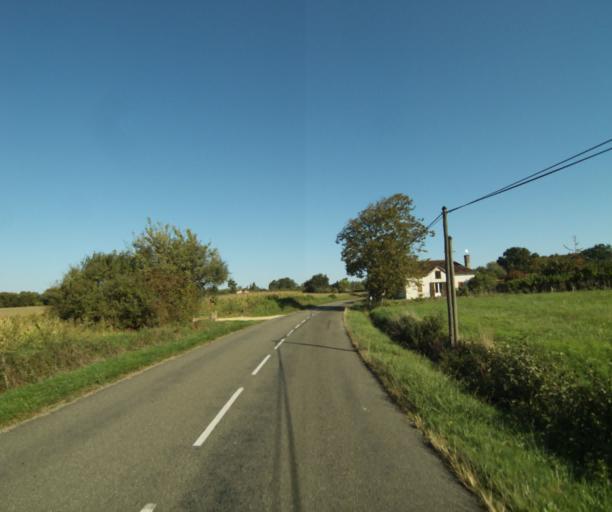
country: FR
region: Aquitaine
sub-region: Departement des Landes
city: Gabarret
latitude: 43.9389
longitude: 0.0141
